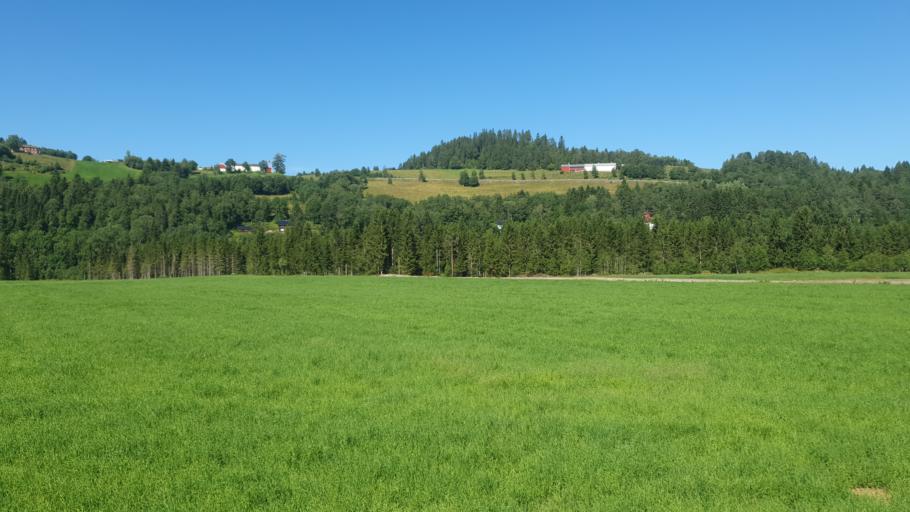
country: NO
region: Sor-Trondelag
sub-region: Meldal
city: Meldal
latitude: 63.1779
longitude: 9.7579
